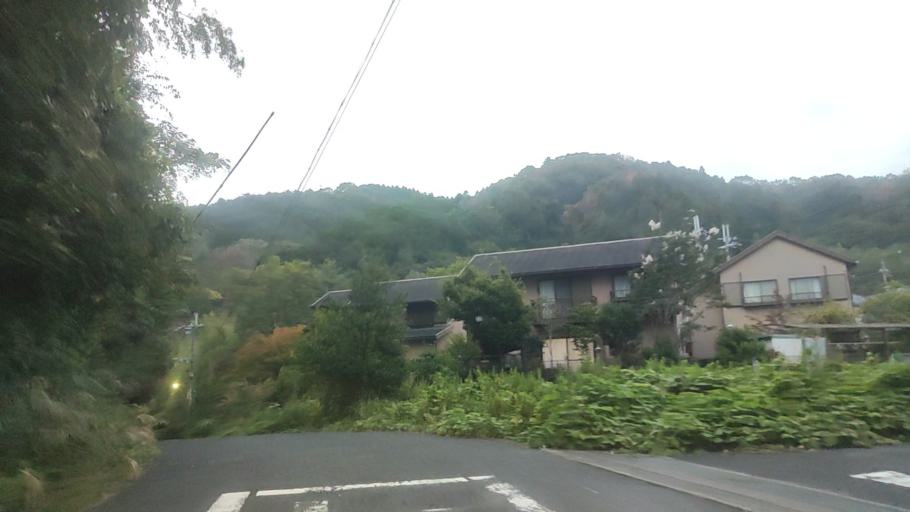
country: JP
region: Wakayama
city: Hashimoto
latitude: 34.3691
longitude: 135.6039
